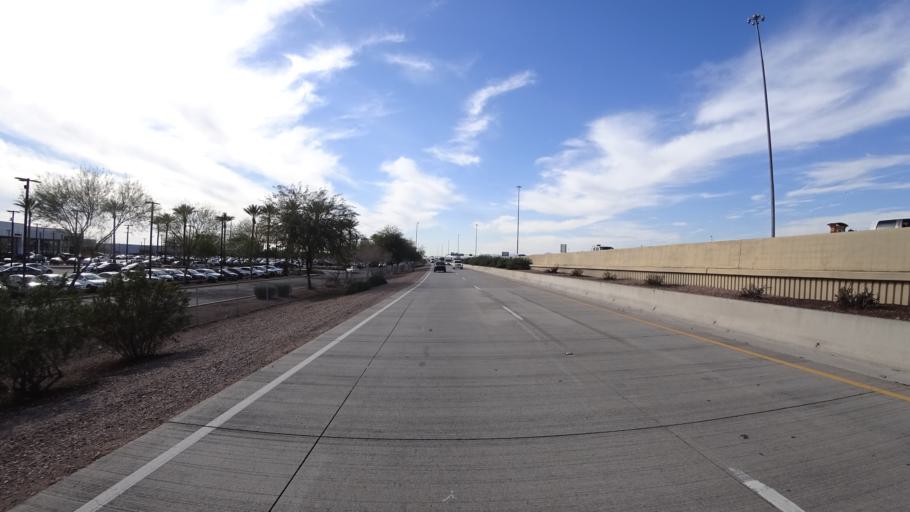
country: US
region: Arizona
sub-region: Maricopa County
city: Tolleson
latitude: 33.4610
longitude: -112.2754
